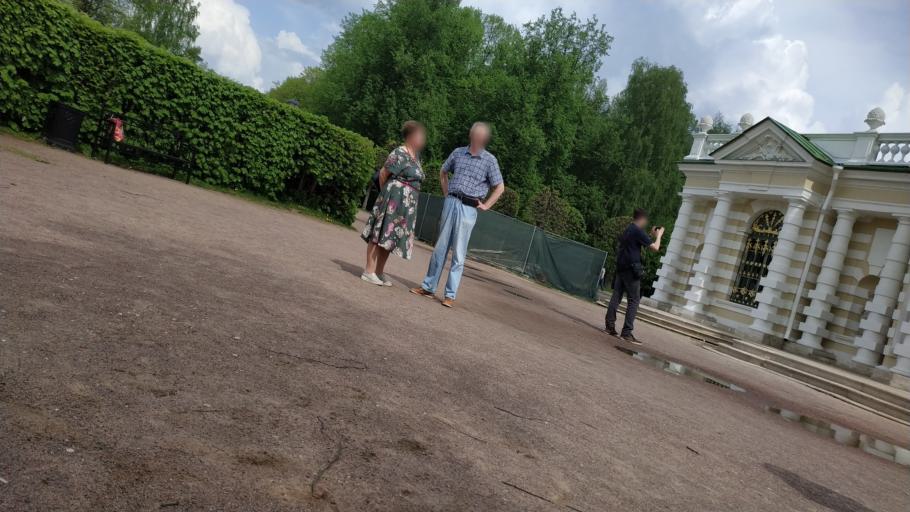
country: RU
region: Moscow
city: Veshnyaki
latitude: 55.7351
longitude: 37.8100
